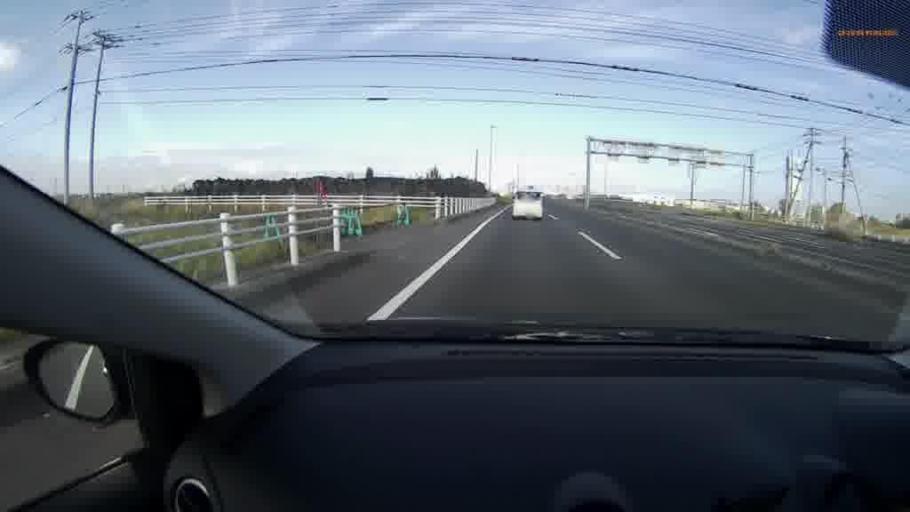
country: JP
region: Hokkaido
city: Kushiro
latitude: 43.0028
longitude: 144.4191
